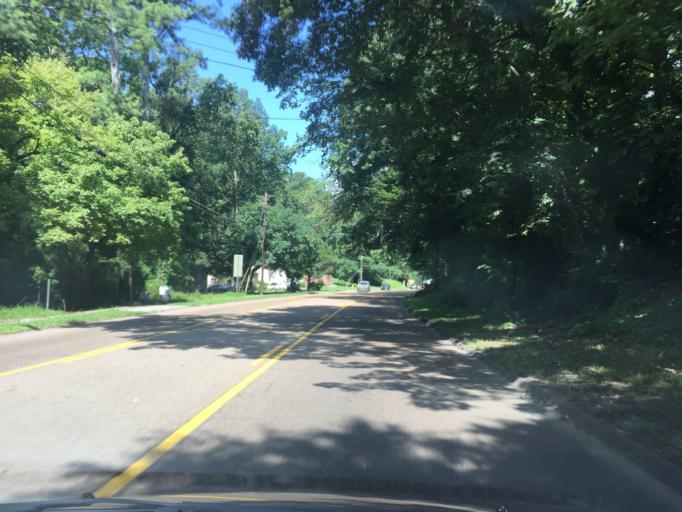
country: US
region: Tennessee
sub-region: Hamilton County
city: East Chattanooga
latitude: 35.0455
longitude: -85.2324
